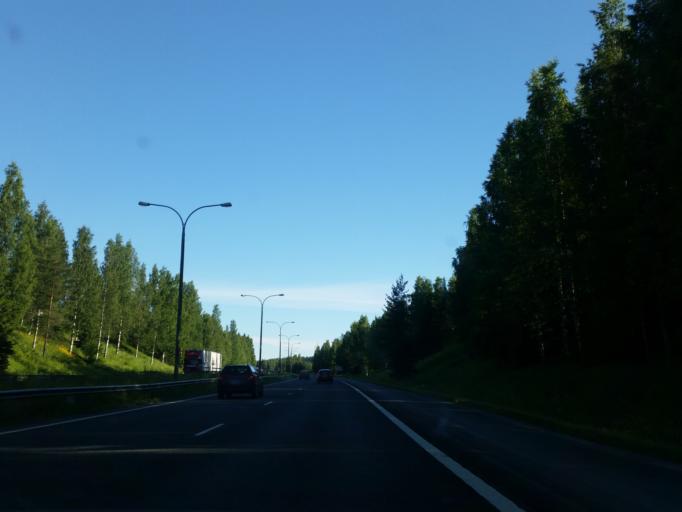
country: FI
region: Northern Savo
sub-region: Kuopio
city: Kuopio
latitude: 62.8696
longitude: 27.6192
